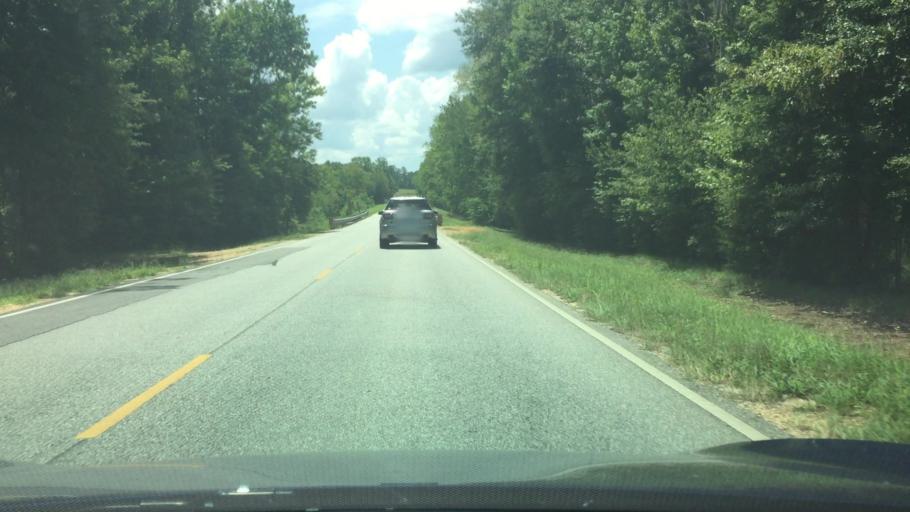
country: US
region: Alabama
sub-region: Montgomery County
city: Pike Road
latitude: 32.2229
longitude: -86.0913
